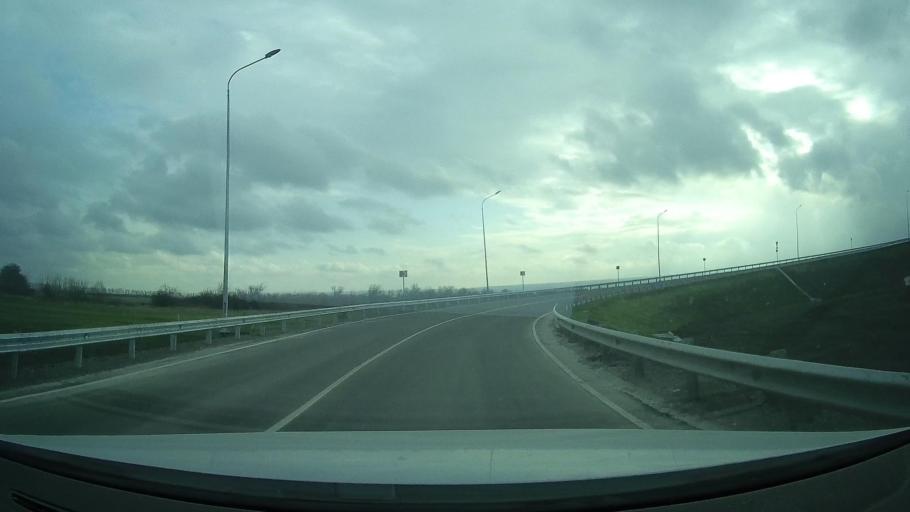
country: RU
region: Rostov
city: Grushevskaya
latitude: 47.4939
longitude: 39.9526
